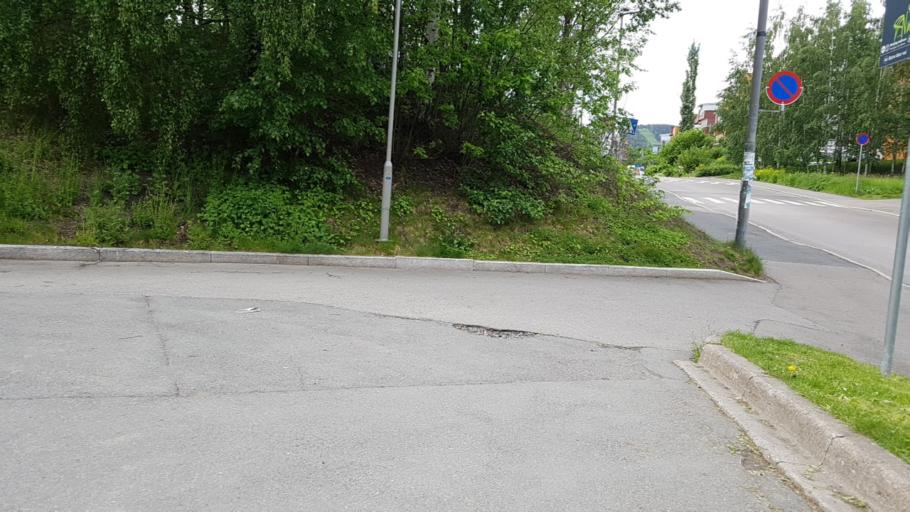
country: NO
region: Oslo
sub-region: Oslo
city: Oslo
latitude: 59.9363
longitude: 10.8312
